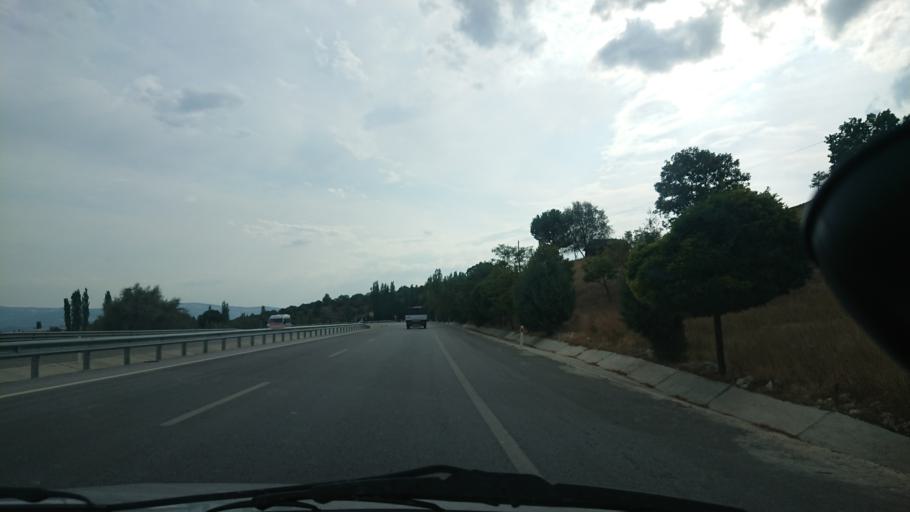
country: TR
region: Kuetahya
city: Gediz
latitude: 39.0167
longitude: 29.4116
